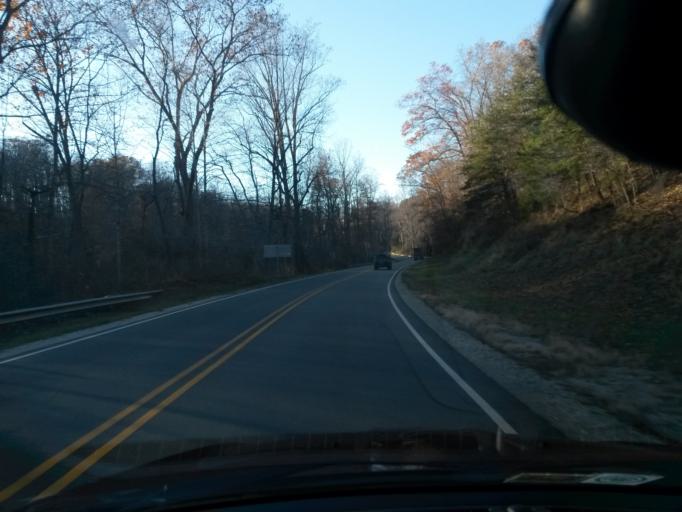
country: US
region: Virginia
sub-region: Amherst County
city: Amherst
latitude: 37.6126
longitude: -79.0841
